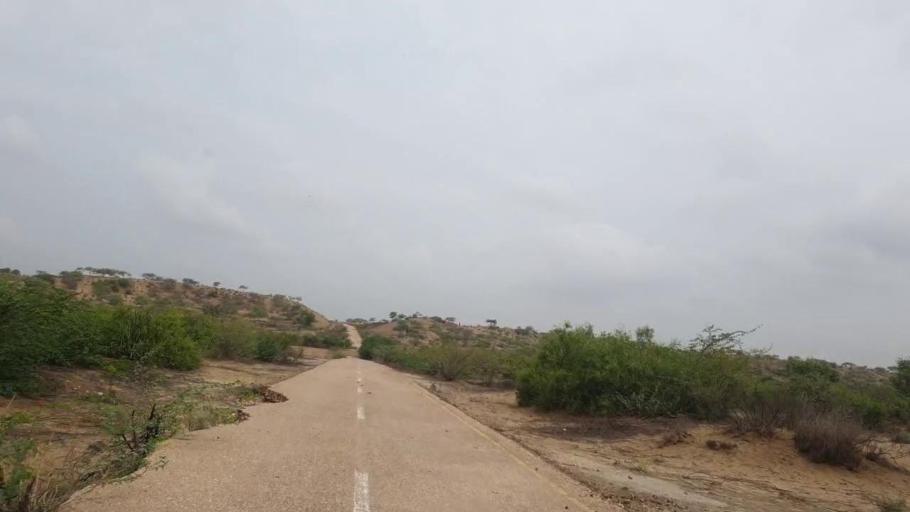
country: PK
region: Sindh
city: Naukot
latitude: 24.6285
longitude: 69.3562
